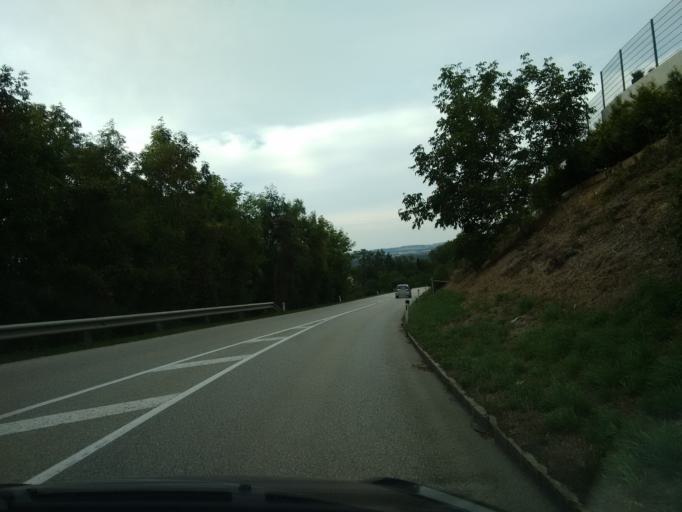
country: AT
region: Upper Austria
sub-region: Wels-Land
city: Marchtrenk
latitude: 48.1566
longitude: 14.1259
